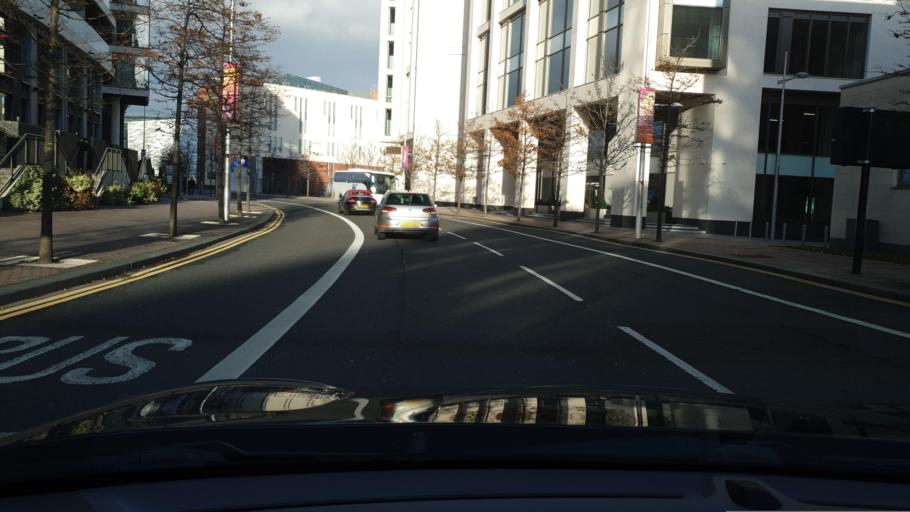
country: GB
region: Northern Ireland
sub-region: City of Belfast
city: Belfast
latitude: 54.6044
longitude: -5.9112
